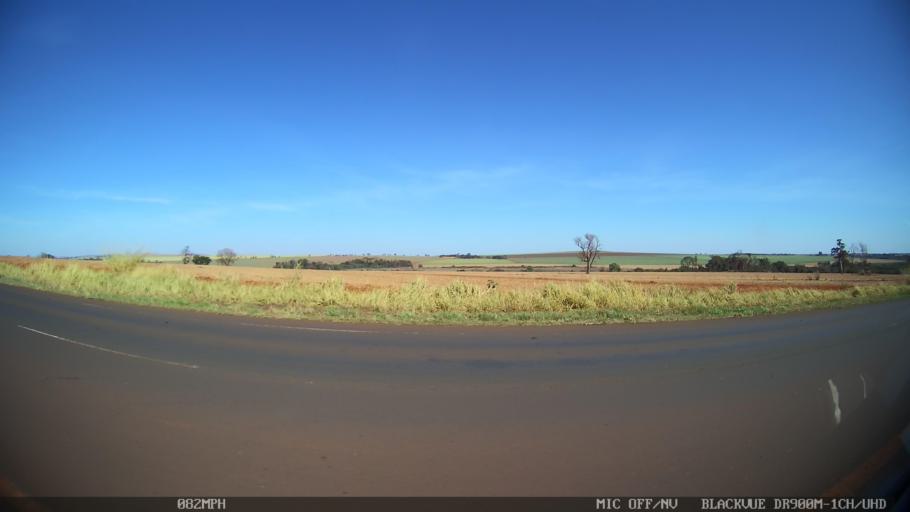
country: BR
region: Sao Paulo
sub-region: Ipua
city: Ipua
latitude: -20.4546
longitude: -48.1638
